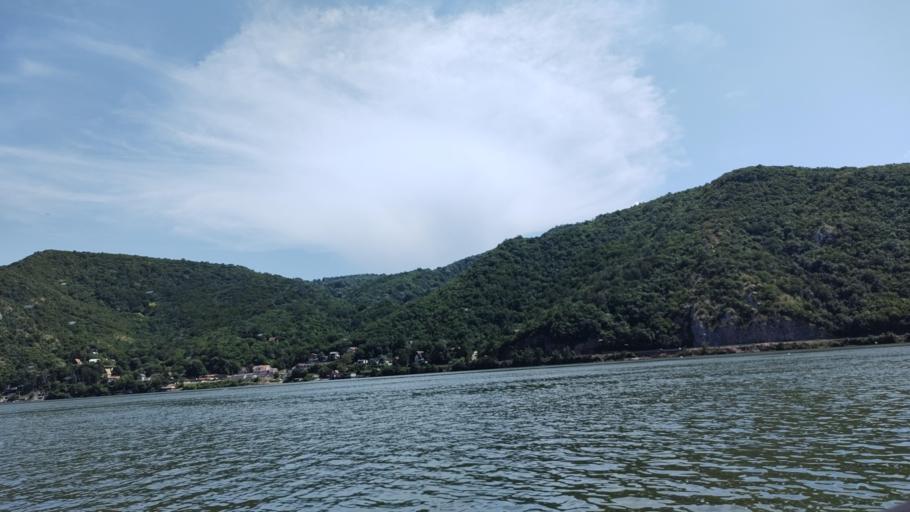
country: RO
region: Caras-Severin
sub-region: Comuna Pescari
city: Coronini
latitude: 44.6651
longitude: 21.6826
